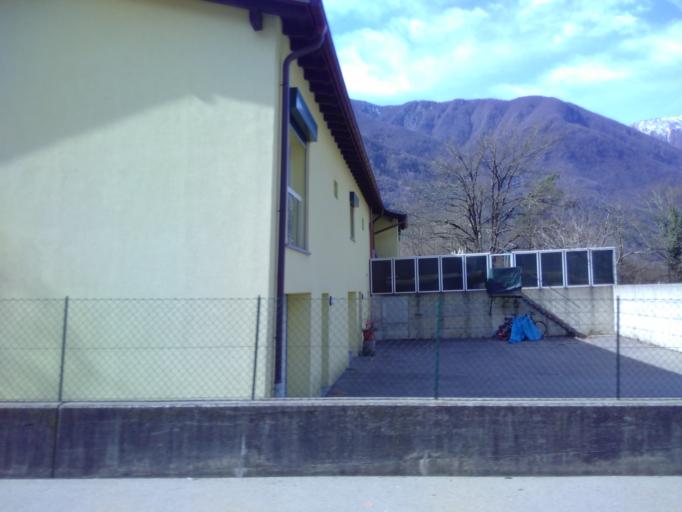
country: CH
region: Ticino
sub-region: Locarno District
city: Verscio
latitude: 46.2271
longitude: 8.7401
